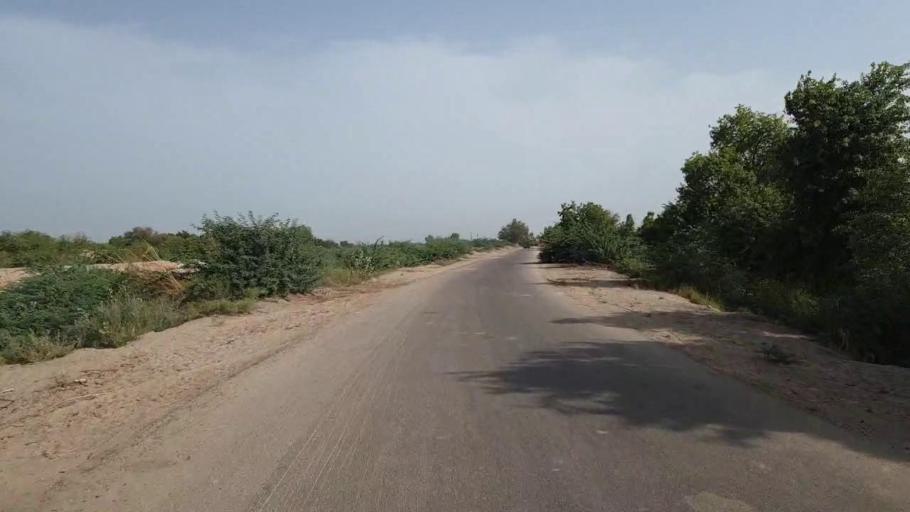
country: PK
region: Sindh
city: Sakrand
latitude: 26.2655
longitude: 68.2813
